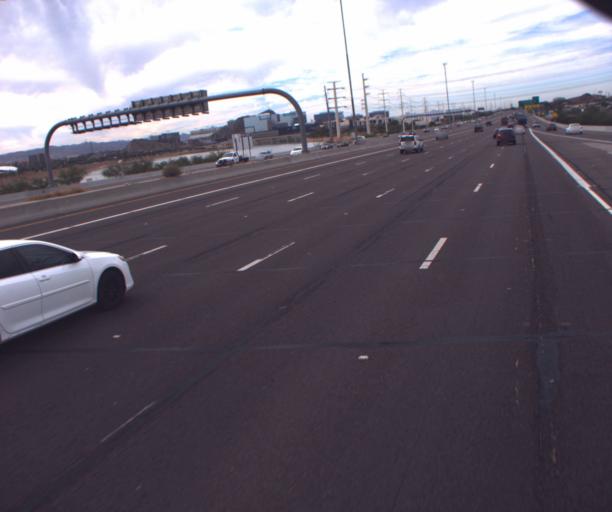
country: US
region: Arizona
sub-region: Maricopa County
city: Tempe
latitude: 33.4362
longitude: -111.9127
